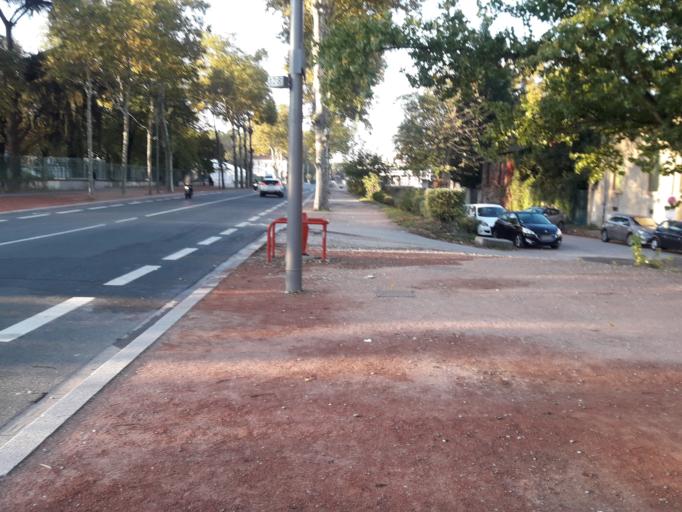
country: FR
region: Rhone-Alpes
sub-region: Departement du Rhone
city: La Mulatiere
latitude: 45.7262
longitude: 4.8304
